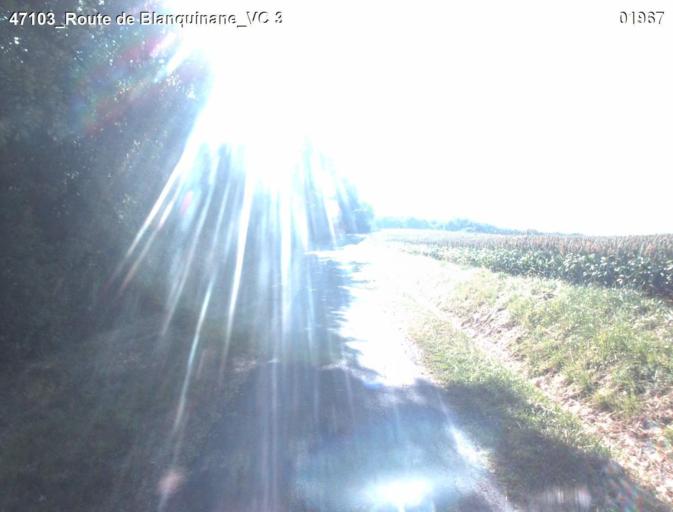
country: FR
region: Aquitaine
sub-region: Departement du Lot-et-Garonne
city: Nerac
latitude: 44.0854
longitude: 0.3416
